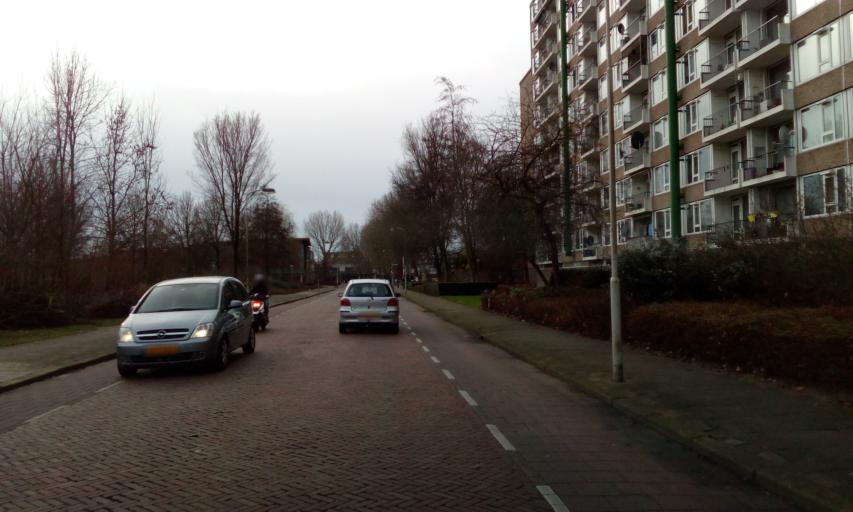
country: NL
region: South Holland
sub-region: Gemeente Gorinchem
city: Gorinchem
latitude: 51.8399
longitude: 4.9517
